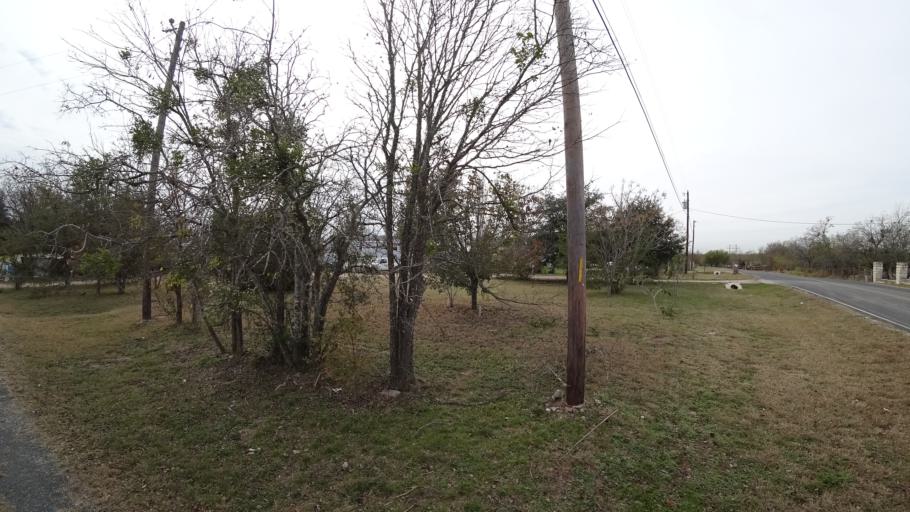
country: US
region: Texas
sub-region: Travis County
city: Garfield
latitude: 30.1416
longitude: -97.5758
